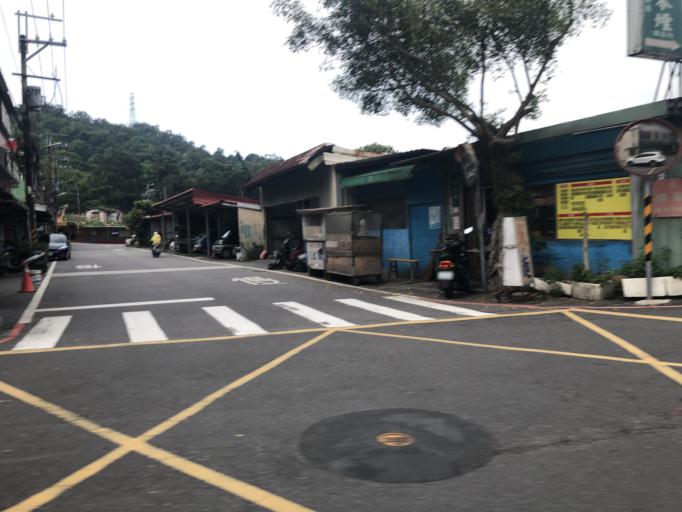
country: TW
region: Taiwan
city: Daxi
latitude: 24.9079
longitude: 121.3599
